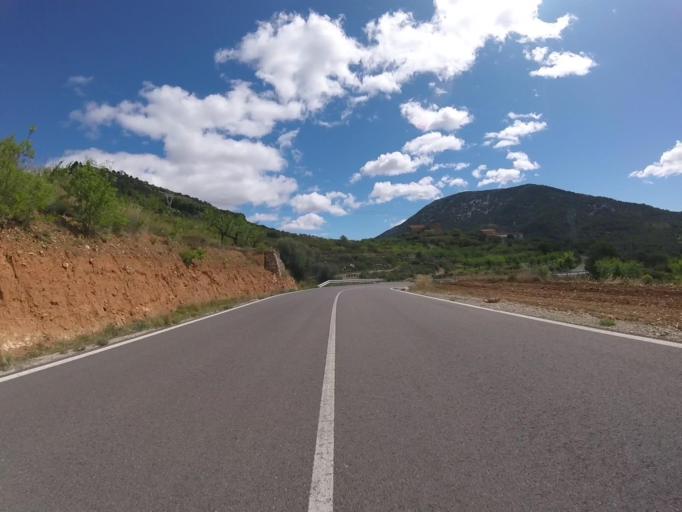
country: ES
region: Valencia
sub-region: Provincia de Castello
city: Culla
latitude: 40.2954
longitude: -0.1136
